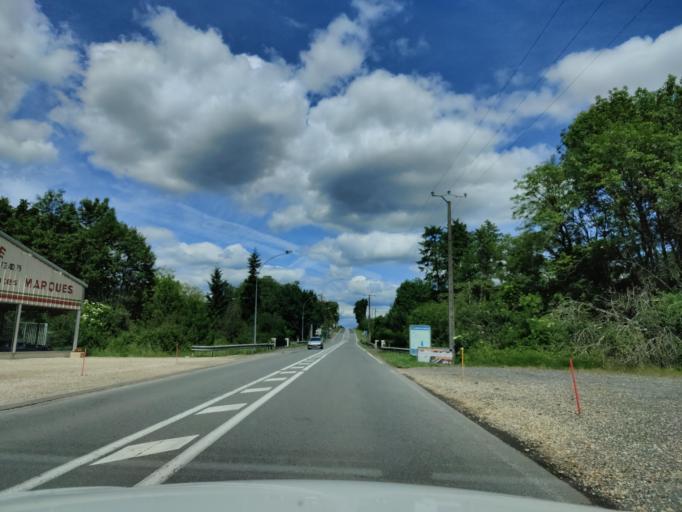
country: FR
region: Centre
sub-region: Departement du Cher
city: Henrichemont
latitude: 47.3656
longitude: 2.4323
